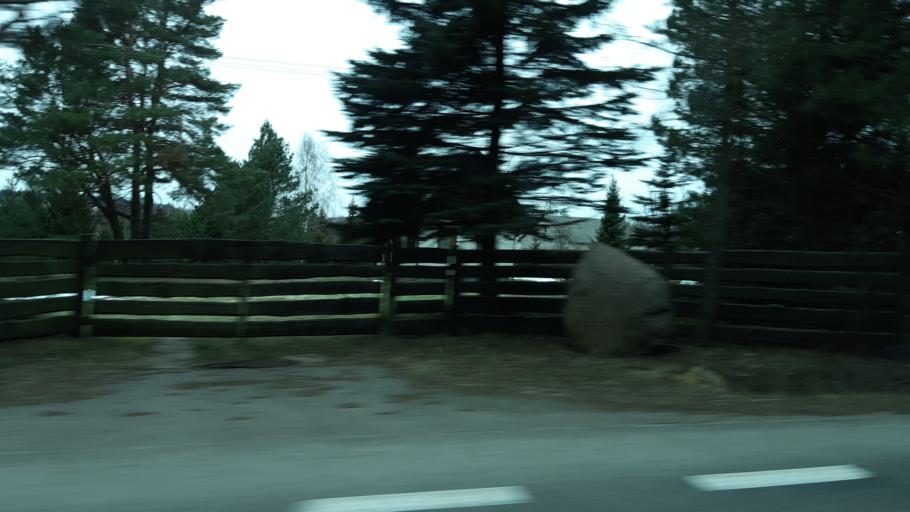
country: PL
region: Podlasie
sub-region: Suwalki
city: Suwalki
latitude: 54.3132
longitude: 22.9592
